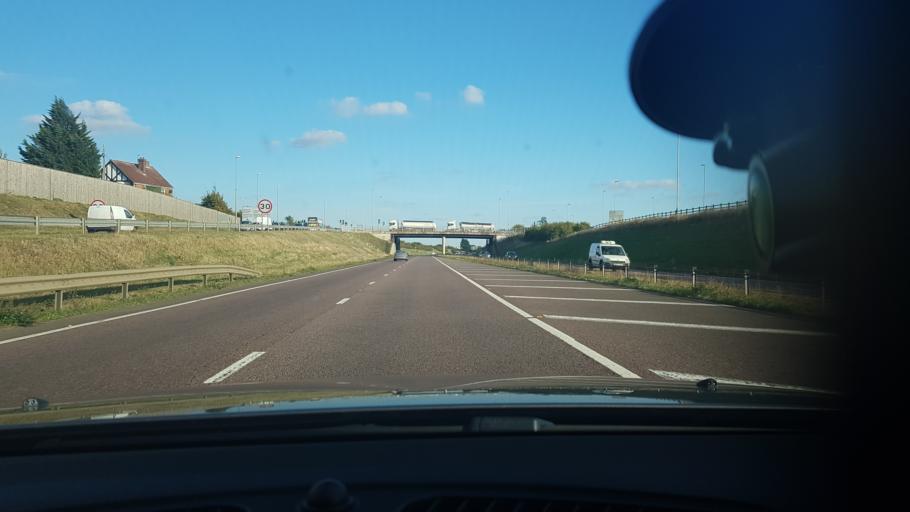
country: GB
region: England
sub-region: Borough of Swindon
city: Broad Blunsdon
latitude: 51.6096
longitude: -1.7917
